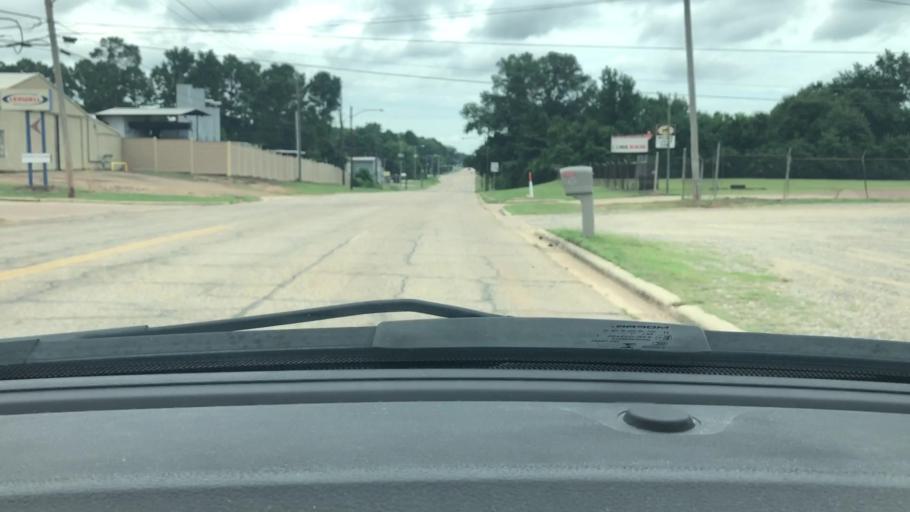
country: US
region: Texas
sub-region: Bowie County
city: Wake Village
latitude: 33.4162
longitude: -94.0803
